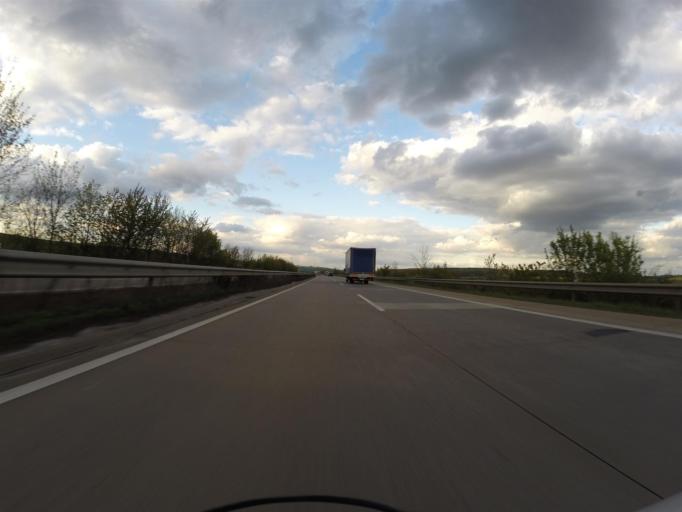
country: DE
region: Rheinland-Pfalz
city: Dreisen
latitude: 49.6144
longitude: 8.0185
